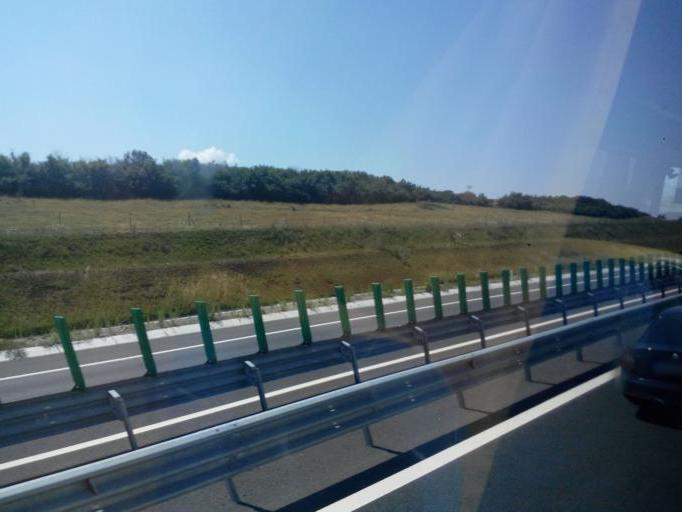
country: RO
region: Alba
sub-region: Comuna Sibot
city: Sibot
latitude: 45.9279
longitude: 23.3594
